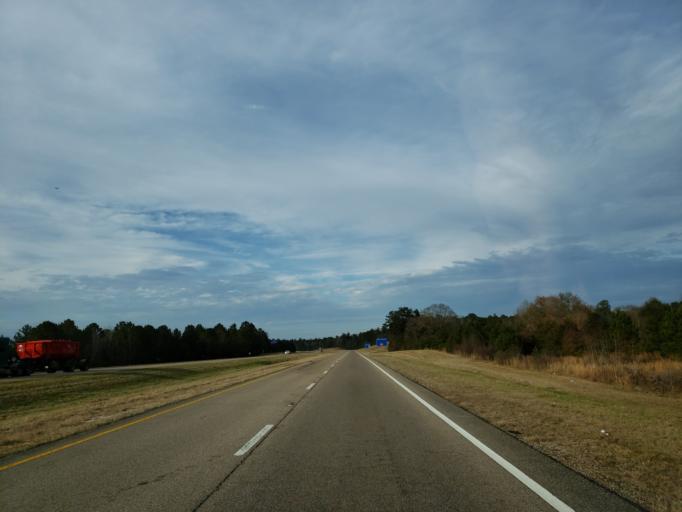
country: US
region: Mississippi
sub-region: Wayne County
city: Waynesboro
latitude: 31.6895
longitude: -88.6173
